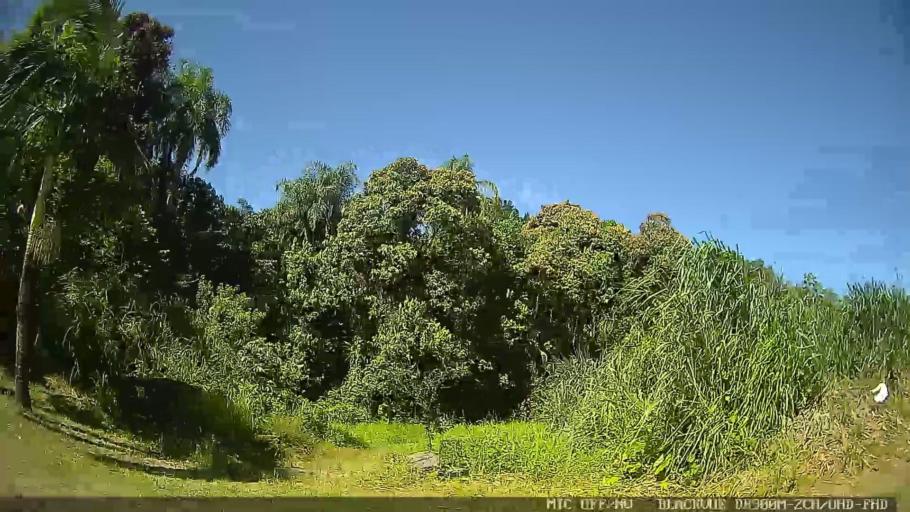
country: BR
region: Sao Paulo
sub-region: Iguape
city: Iguape
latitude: -24.6935
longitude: -47.5670
